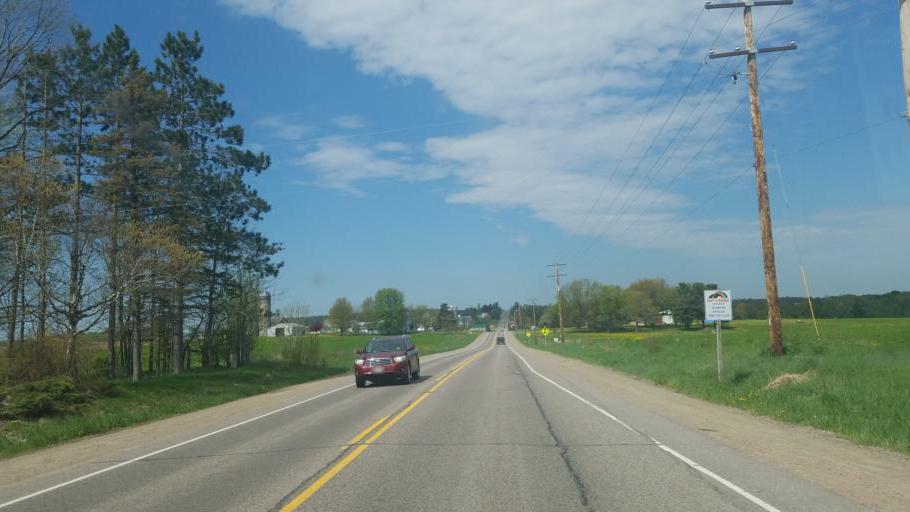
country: US
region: Wisconsin
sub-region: Clark County
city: Loyal
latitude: 44.5825
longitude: -90.3966
